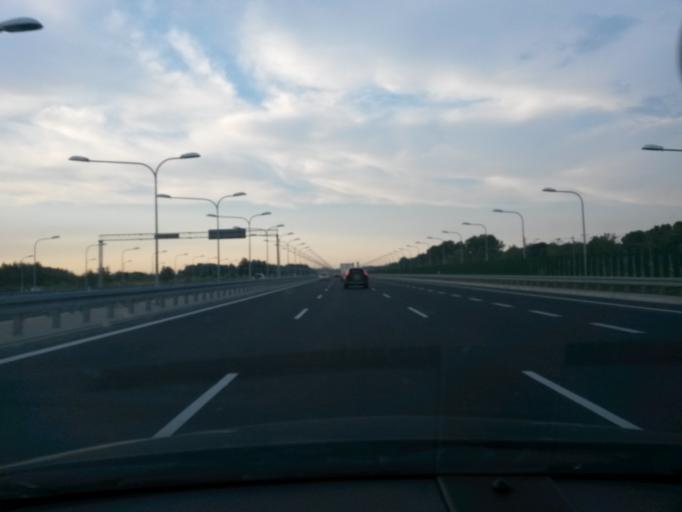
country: PL
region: Masovian Voivodeship
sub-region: Powiat piaseczynski
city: Mysiadlo
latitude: 52.1430
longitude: 20.9889
